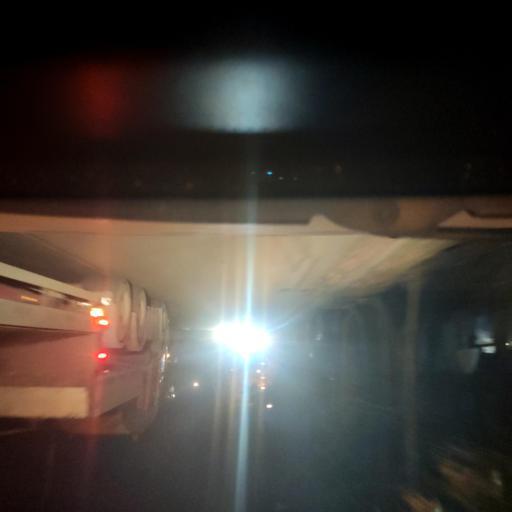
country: RU
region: Perm
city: Polazna
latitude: 58.1326
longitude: 56.3820
